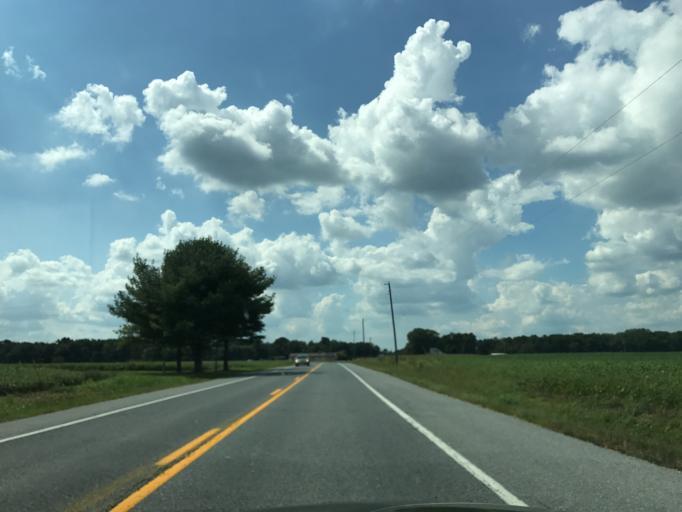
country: US
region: Delaware
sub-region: Kent County
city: Clayton
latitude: 39.1931
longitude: -75.8269
